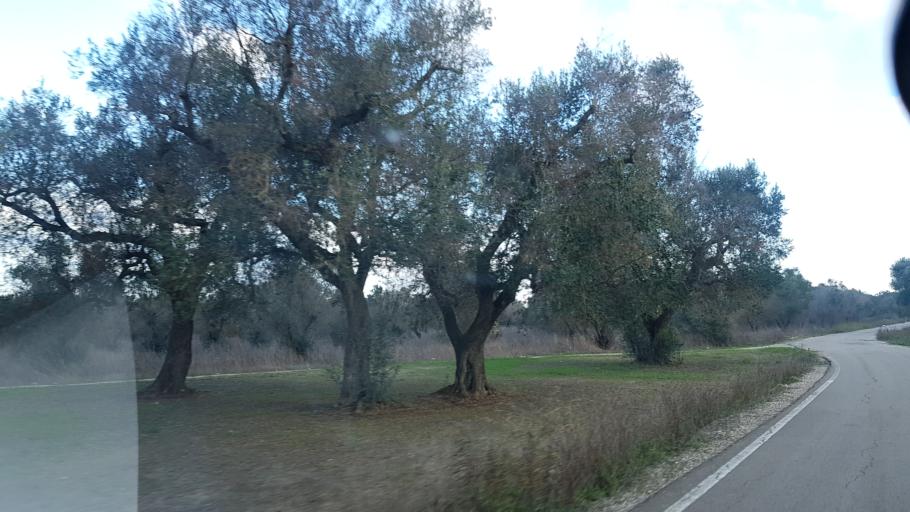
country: IT
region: Apulia
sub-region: Provincia di Brindisi
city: San Pietro Vernotico
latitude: 40.5147
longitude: 18.0144
